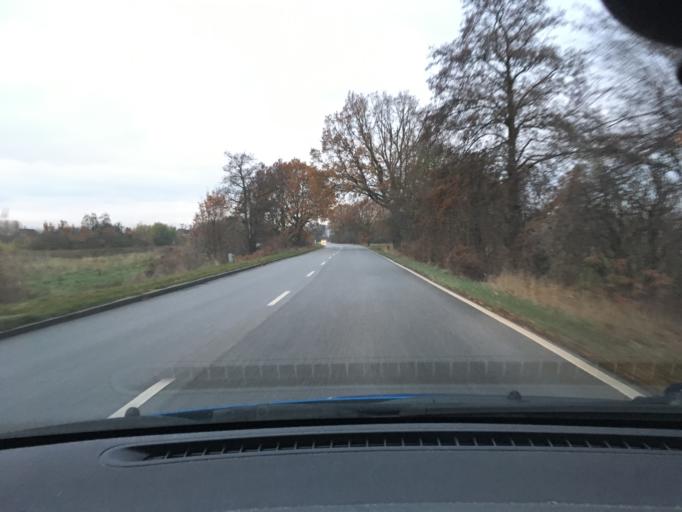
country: DE
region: Lower Saxony
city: Drage
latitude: 53.4224
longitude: 10.2095
